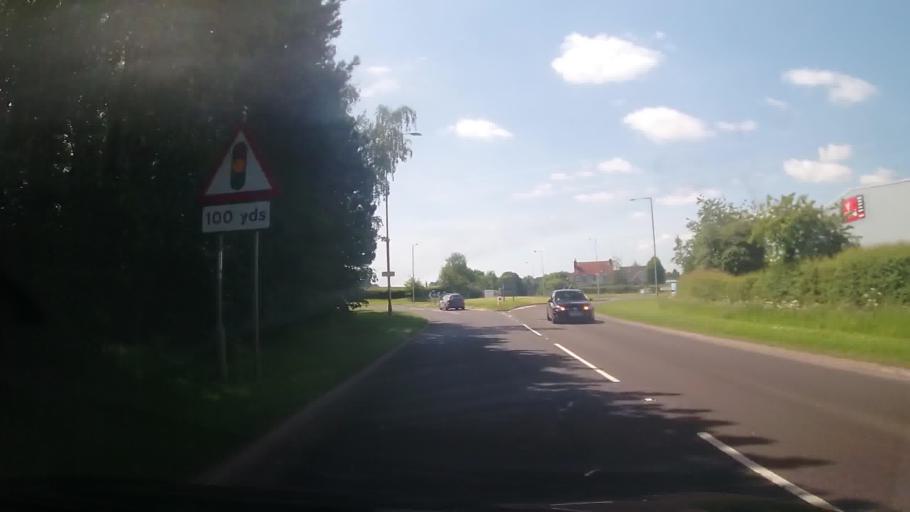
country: GB
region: England
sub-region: Shropshire
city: Ludlow
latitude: 52.3661
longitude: -2.6934
